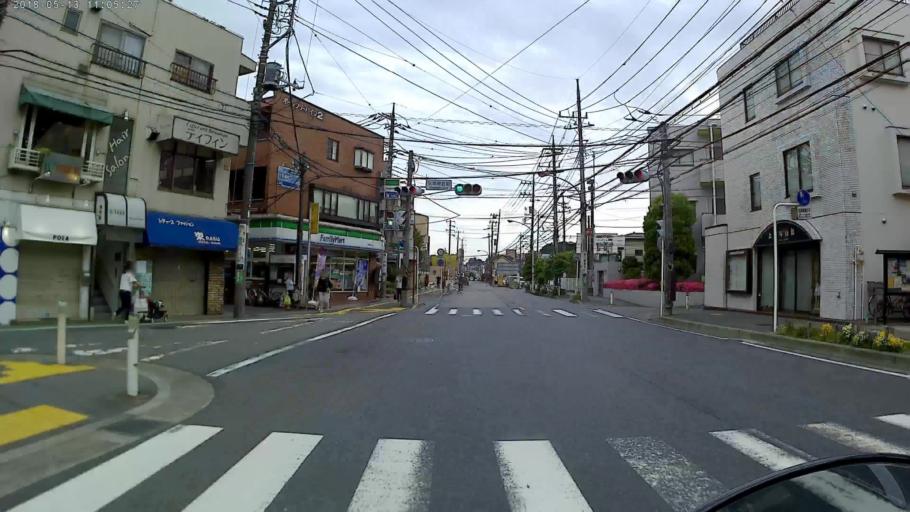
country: JP
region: Tokyo
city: Chofugaoka
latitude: 35.5963
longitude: 139.6131
